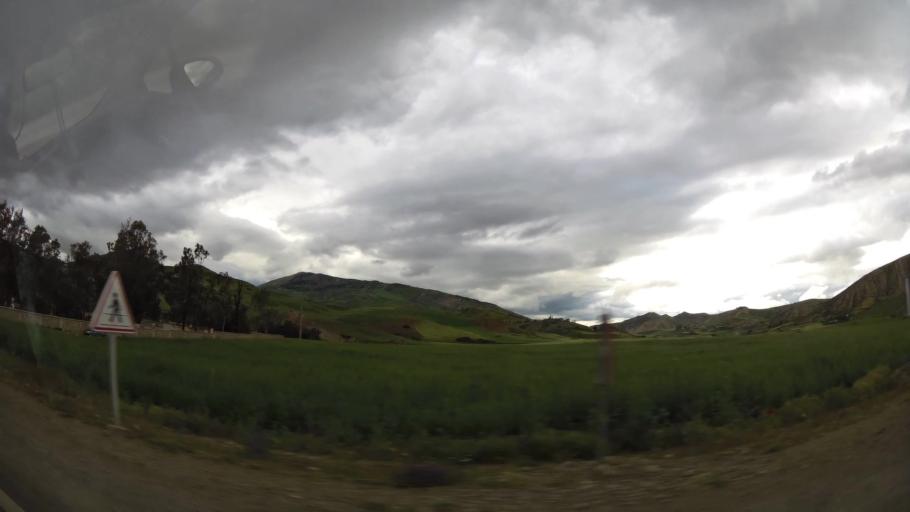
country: MA
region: Taza-Al Hoceima-Taounate
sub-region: Taza
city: Taza
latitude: 34.3543
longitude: -3.9199
